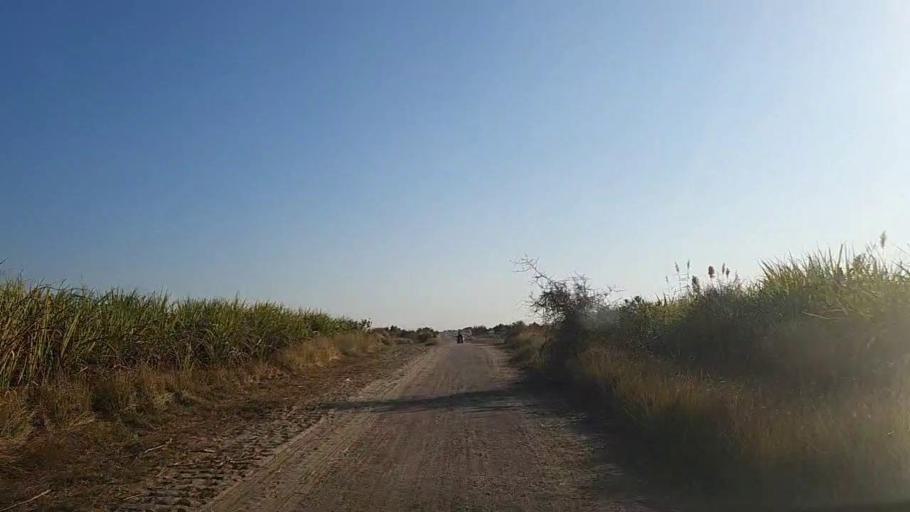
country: PK
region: Sindh
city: Khadro
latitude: 26.2682
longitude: 68.8602
